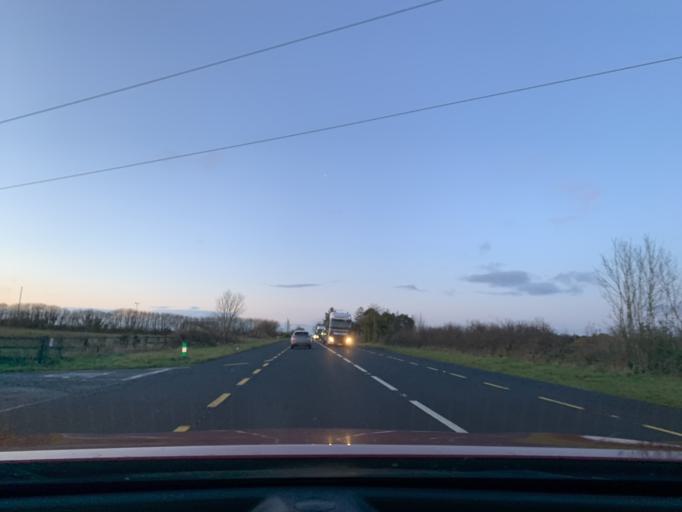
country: IE
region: Connaught
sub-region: County Leitrim
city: Carrick-on-Shannon
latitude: 53.8925
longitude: -7.9478
